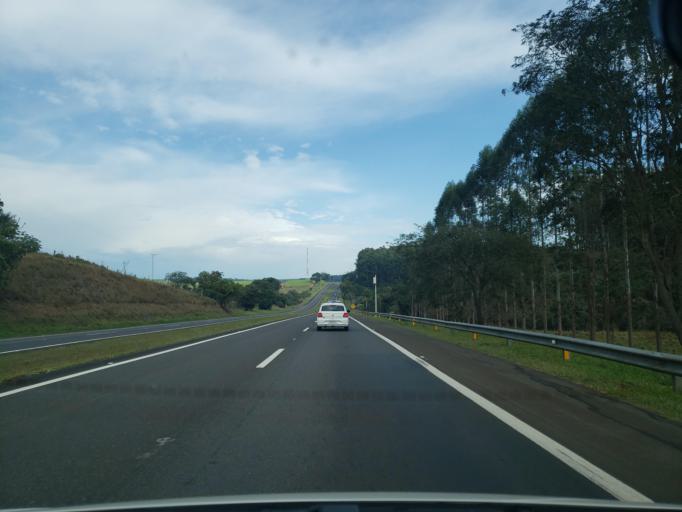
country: BR
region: Sao Paulo
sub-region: Itirapina
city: Itirapina
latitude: -22.2746
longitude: -47.9634
